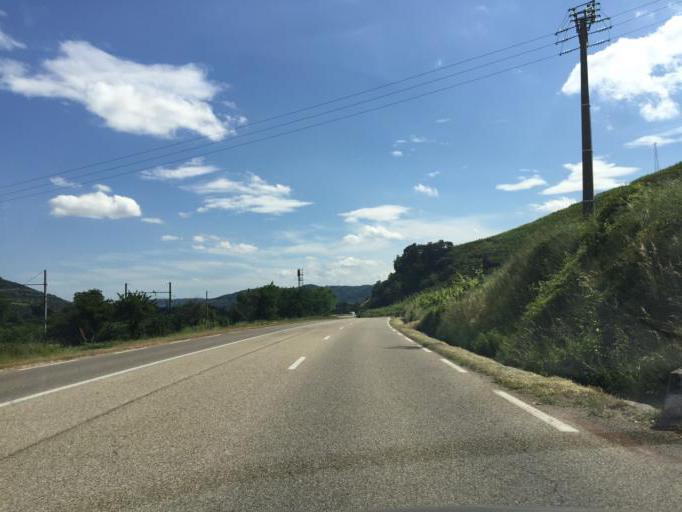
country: FR
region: Rhone-Alpes
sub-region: Departement de la Drome
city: Saint-Vallier
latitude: 45.1531
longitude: 4.8147
